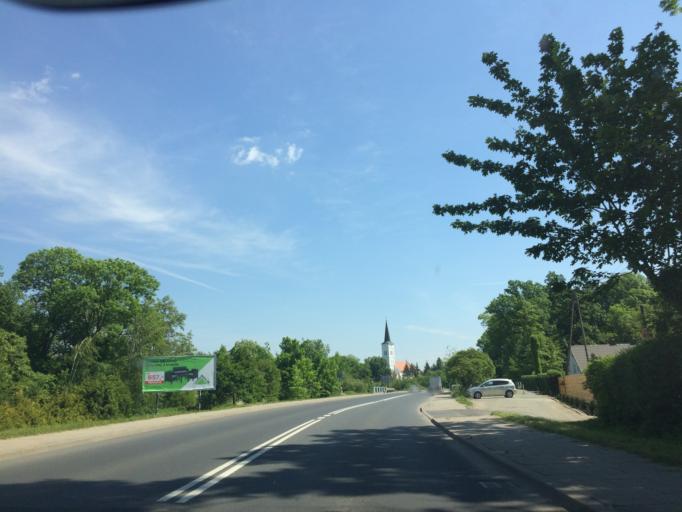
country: PL
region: Lower Silesian Voivodeship
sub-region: Powiat wroclawski
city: Gniechowice
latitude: 50.9866
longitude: 16.8279
